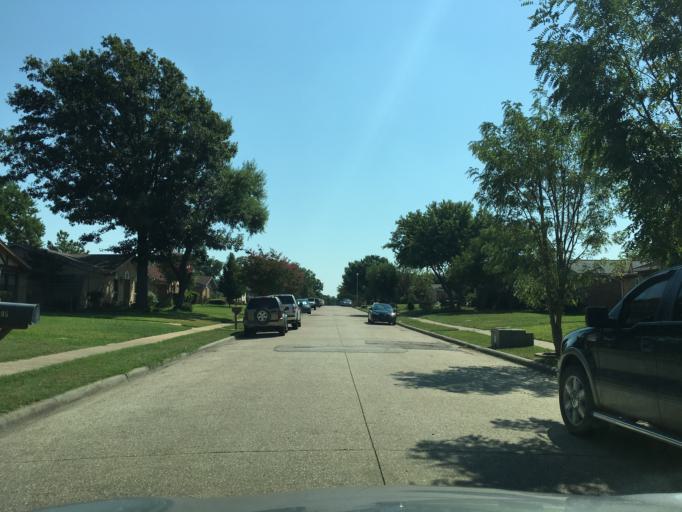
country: US
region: Texas
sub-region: Dallas County
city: Garland
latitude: 32.9339
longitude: -96.6551
